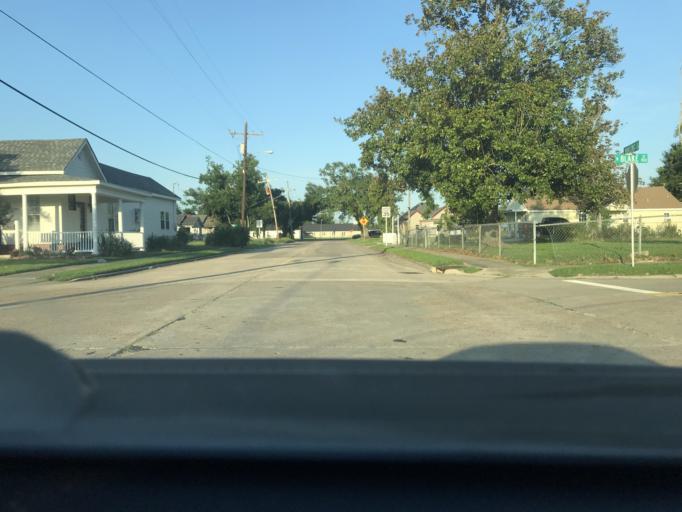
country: US
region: Louisiana
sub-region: Calcasieu Parish
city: Lake Charles
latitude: 30.2500
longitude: -93.1988
